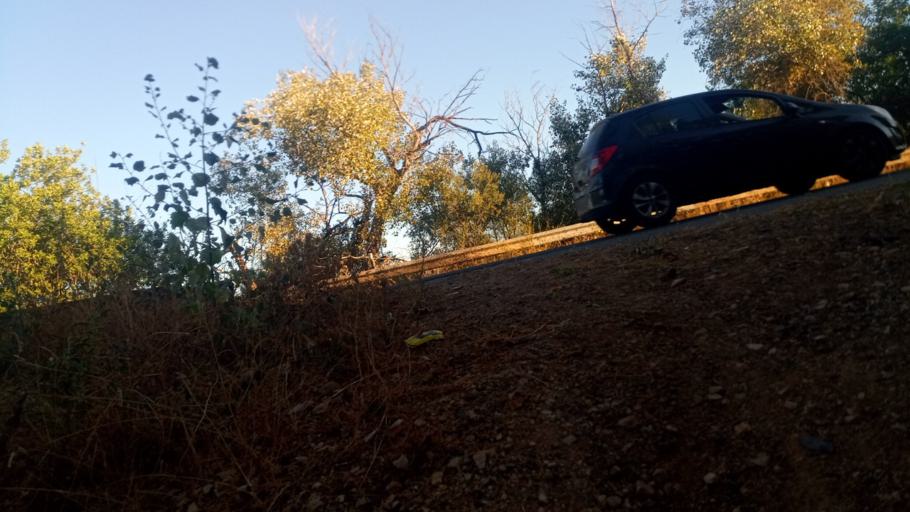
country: PT
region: Faro
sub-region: Tavira
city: Tavira
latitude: 37.1458
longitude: -7.6170
